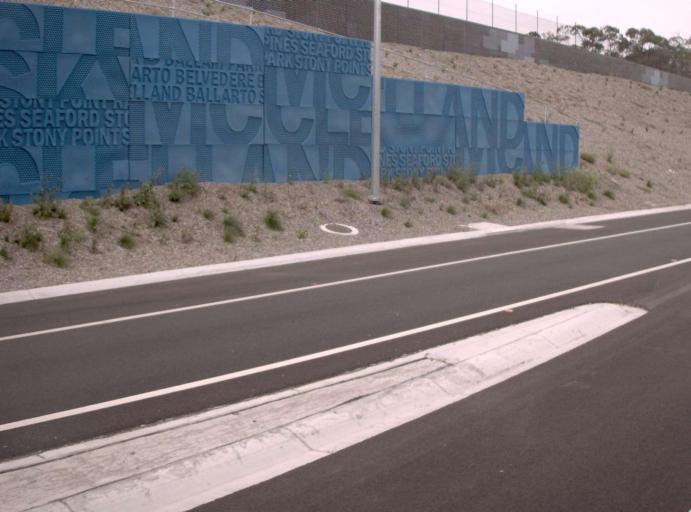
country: AU
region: Victoria
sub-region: Frankston
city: Langwarrin
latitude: -38.1595
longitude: 145.1668
